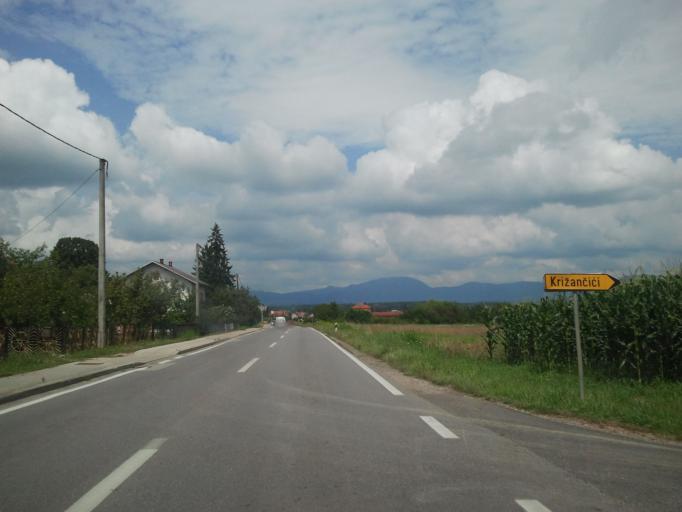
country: HR
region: Zagrebacka
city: Jastrebarsko
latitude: 45.6085
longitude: 15.5977
